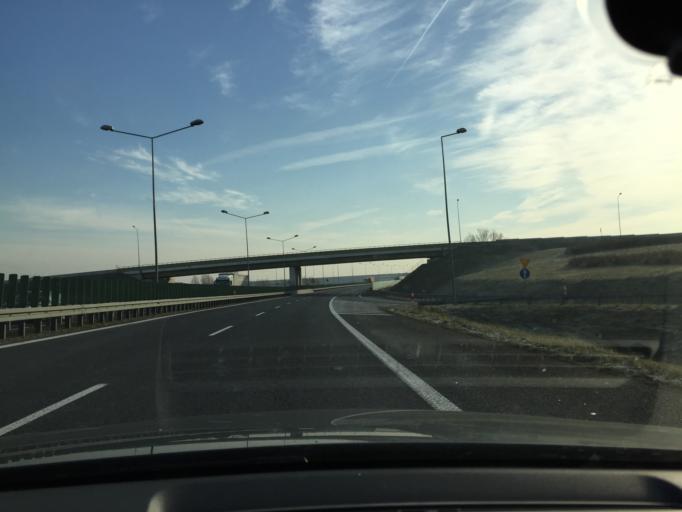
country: PL
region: Silesian Voivodeship
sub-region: Powiat gliwicki
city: Sosnicowice
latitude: 50.3465
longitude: 18.5396
